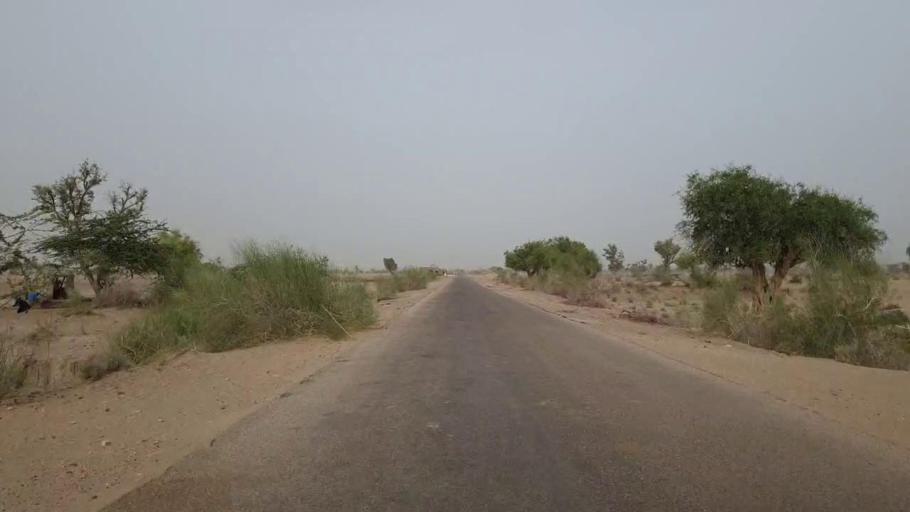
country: PK
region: Sindh
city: Islamkot
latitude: 24.5498
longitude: 70.3578
